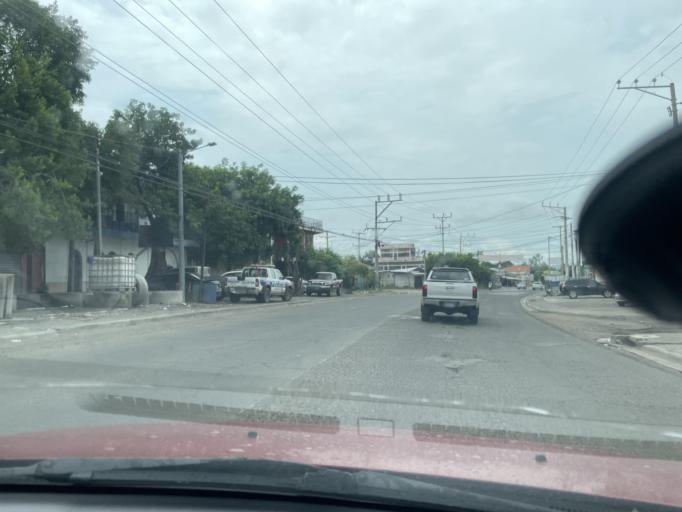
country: SV
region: La Union
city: Santa Rosa de Lima
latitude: 13.6315
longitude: -87.8891
